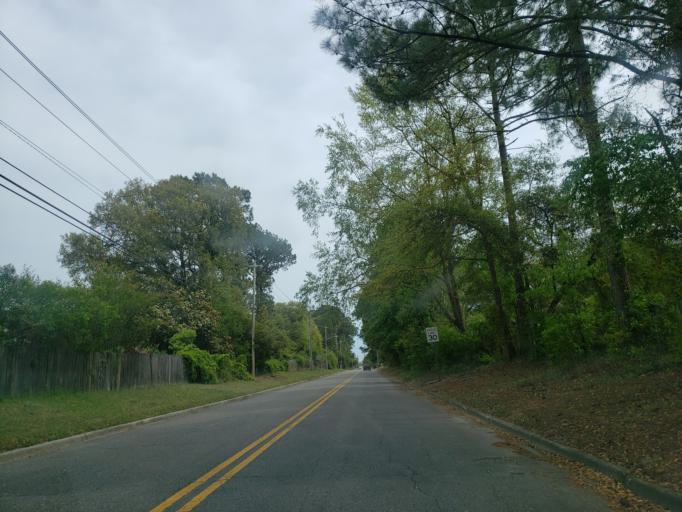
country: US
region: Georgia
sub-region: Chatham County
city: Georgetown
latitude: 31.9917
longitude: -81.1650
